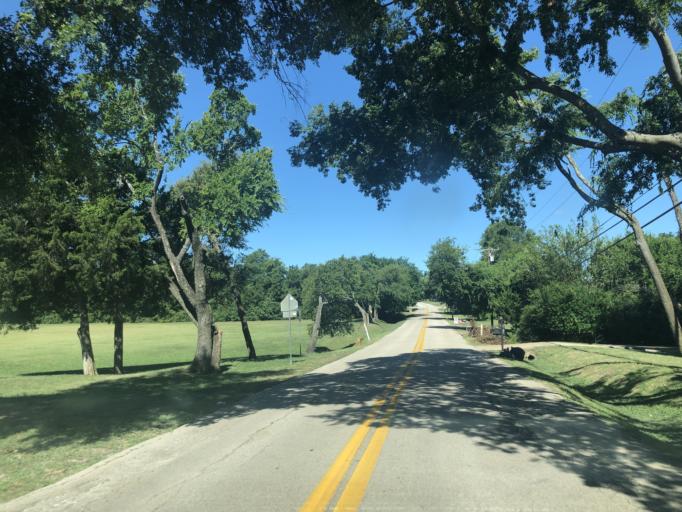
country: US
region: Texas
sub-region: Dallas County
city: Duncanville
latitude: 32.6558
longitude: -96.9331
